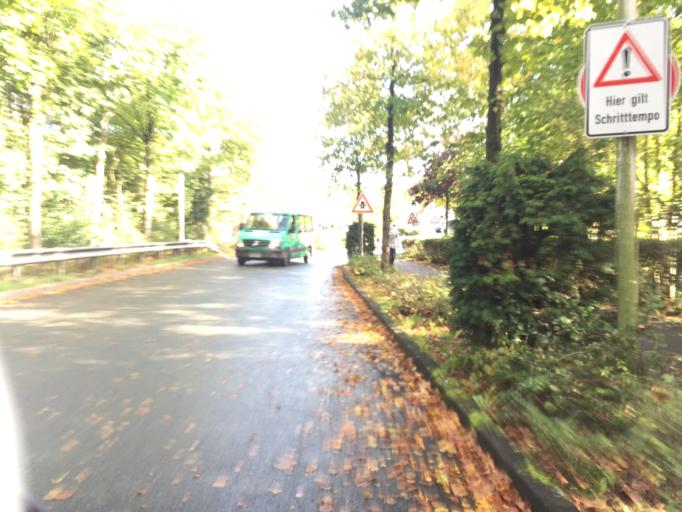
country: DE
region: Schleswig-Holstein
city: Heiligenstedten
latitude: 53.9351
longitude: 9.4966
